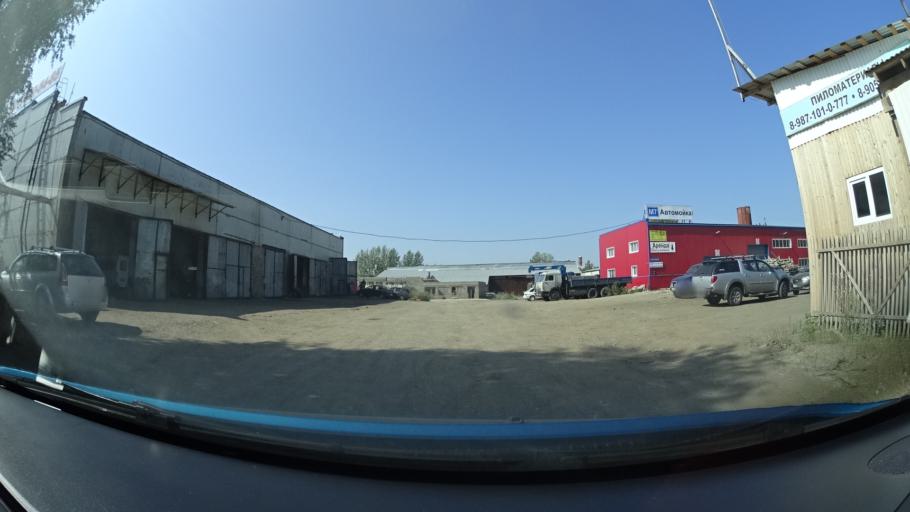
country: RU
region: Bashkortostan
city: Mikhaylovka
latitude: 54.8053
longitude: 55.8494
